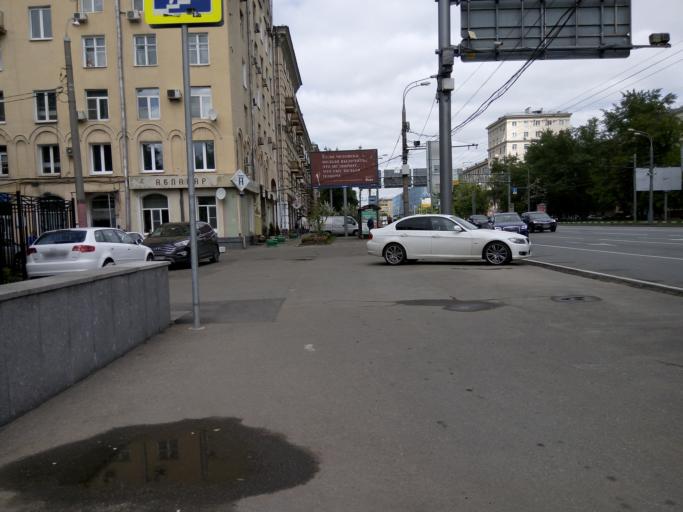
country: RU
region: Moskovskaya
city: Kozhukhovo
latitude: 55.7112
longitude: 37.6653
